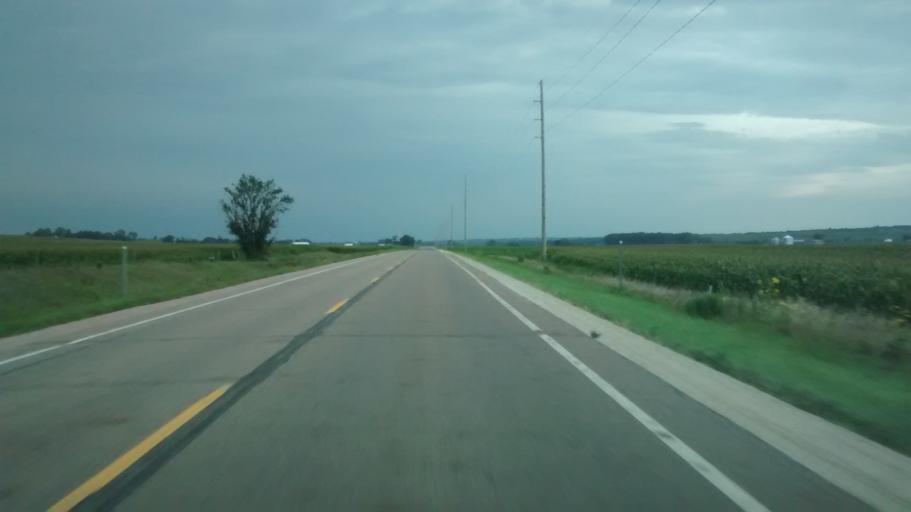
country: US
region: Iowa
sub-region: Plymouth County
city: Kingsley
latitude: 42.5801
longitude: -95.9861
